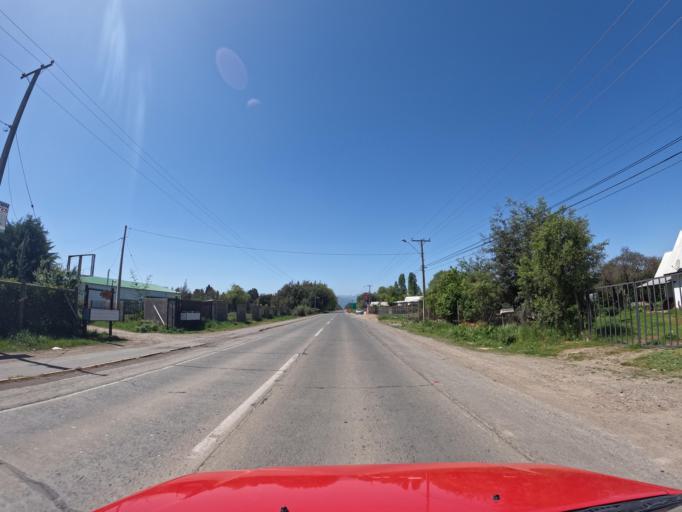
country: CL
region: Maule
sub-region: Provincia de Linares
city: Linares
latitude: -35.8331
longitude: -71.5346
